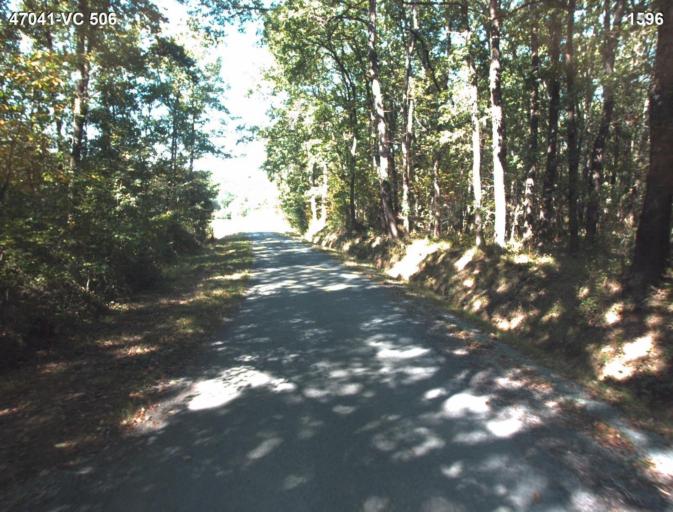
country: FR
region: Aquitaine
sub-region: Departement du Lot-et-Garonne
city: Port-Sainte-Marie
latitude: 44.2022
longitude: 0.3855
